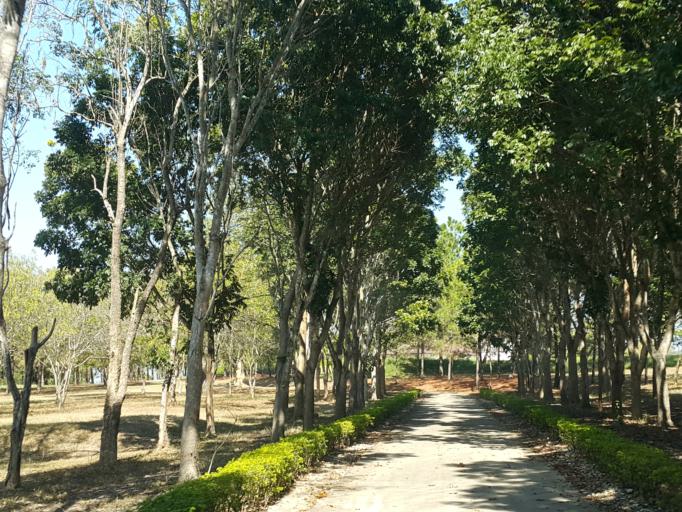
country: TH
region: Chiang Mai
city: Mae Taeng
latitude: 19.0226
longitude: 98.9909
